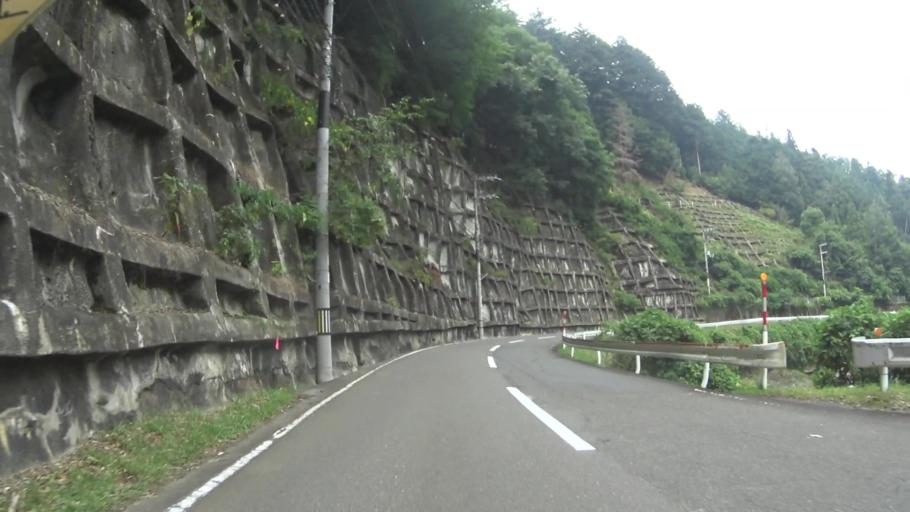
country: JP
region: Kyoto
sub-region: Kyoto-shi
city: Kamigyo-ku
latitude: 35.2029
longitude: 135.7103
